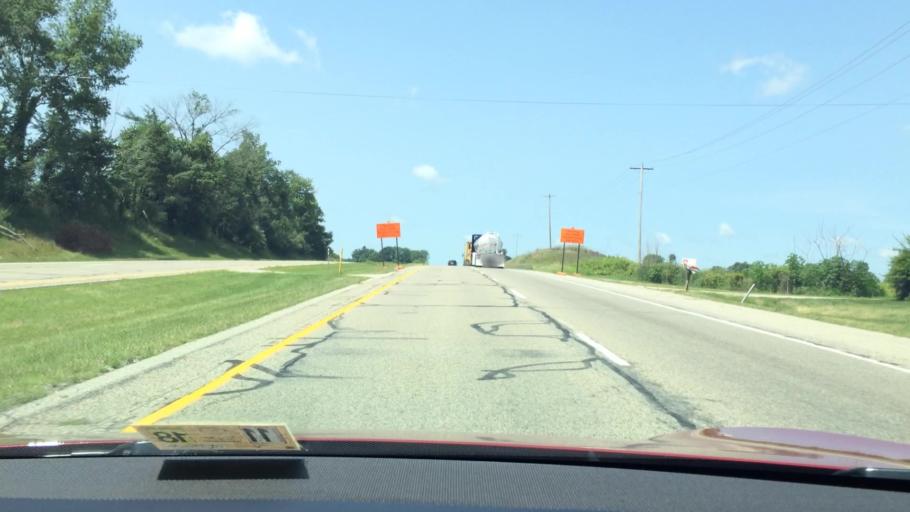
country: US
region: Indiana
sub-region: LaPorte County
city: Hudson Lake
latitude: 41.6726
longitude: -86.5554
